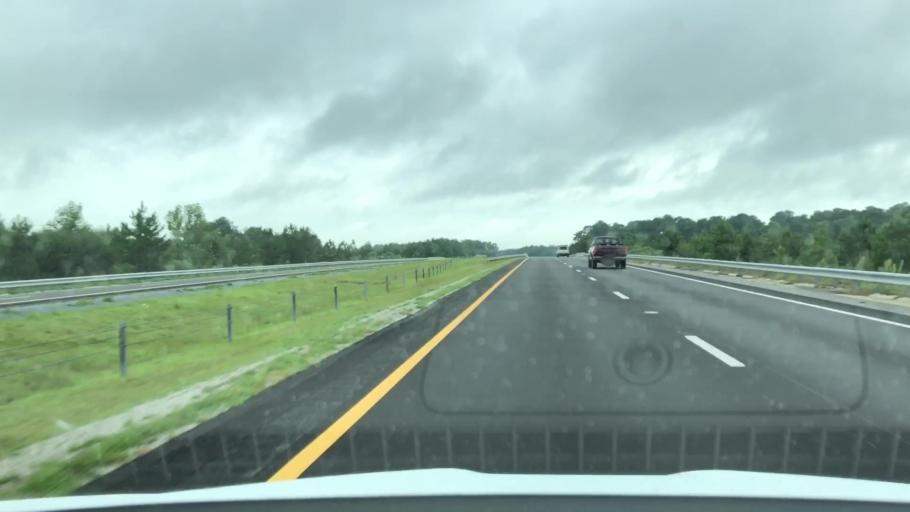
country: US
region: North Carolina
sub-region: Wayne County
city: Fremont
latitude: 35.4674
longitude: -77.9863
